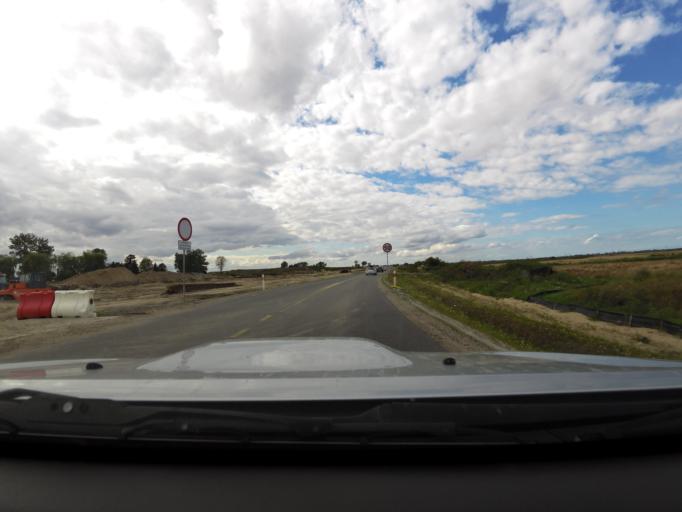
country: PL
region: Pomeranian Voivodeship
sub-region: Powiat nowodworski
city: Nowy Dwor Gdanski
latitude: 54.2267
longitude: 19.0576
